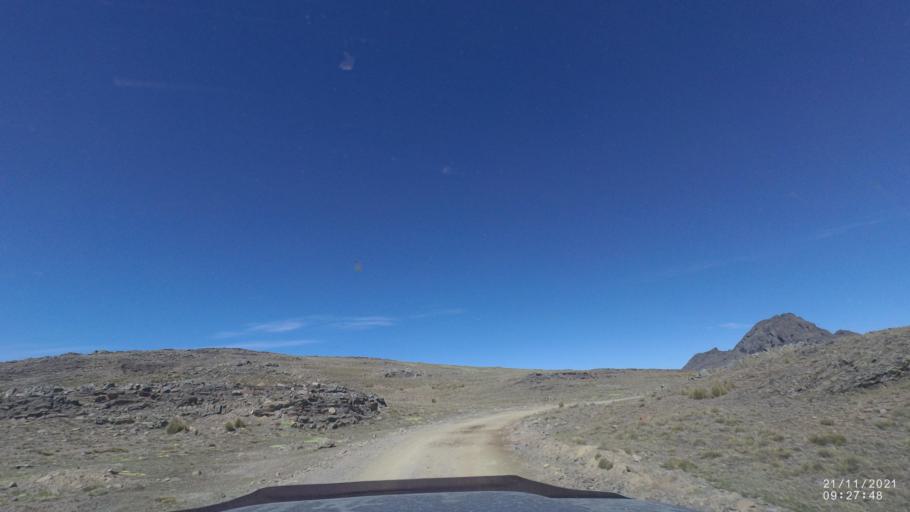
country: BO
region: Cochabamba
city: Cochabamba
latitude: -17.0833
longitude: -66.2518
